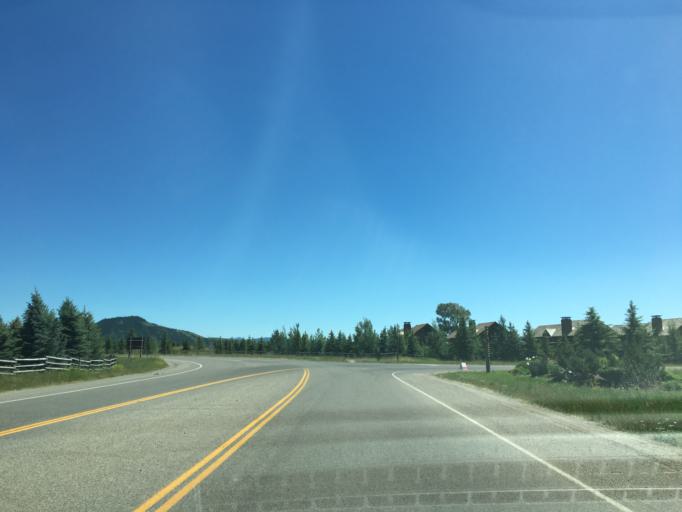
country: US
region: Wyoming
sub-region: Teton County
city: Moose Wilson Road
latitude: 43.5857
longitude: -110.8259
